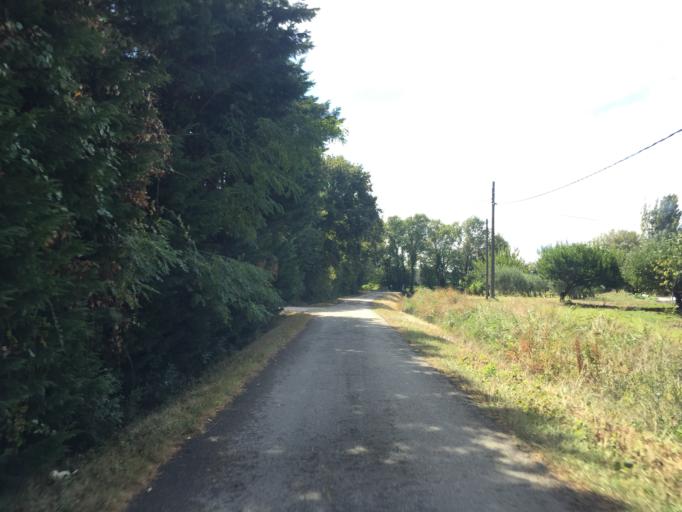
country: FR
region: Provence-Alpes-Cote d'Azur
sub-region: Departement du Vaucluse
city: Caderousse
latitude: 44.1098
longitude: 4.7383
